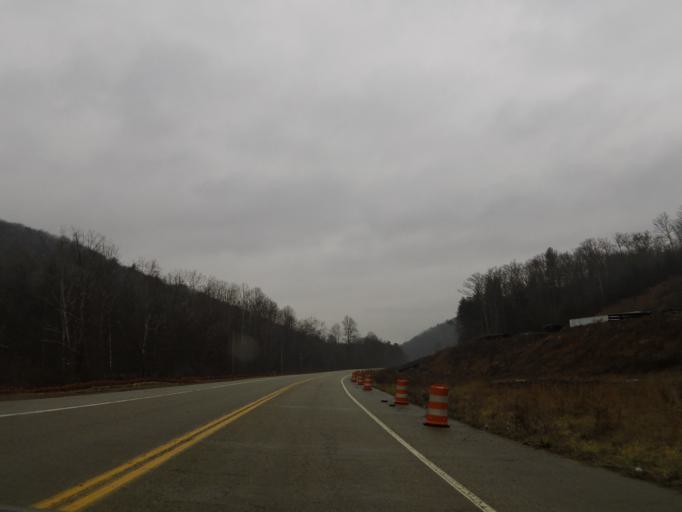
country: US
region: Tennessee
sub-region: Roane County
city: Harriman
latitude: 35.9929
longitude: -84.4960
